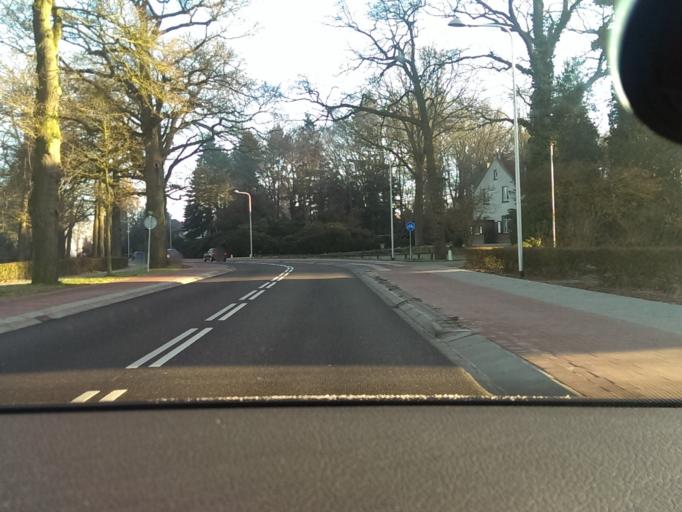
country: NL
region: Overijssel
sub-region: Gemeente Twenterand
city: Den Ham
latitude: 52.5131
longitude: 6.4214
